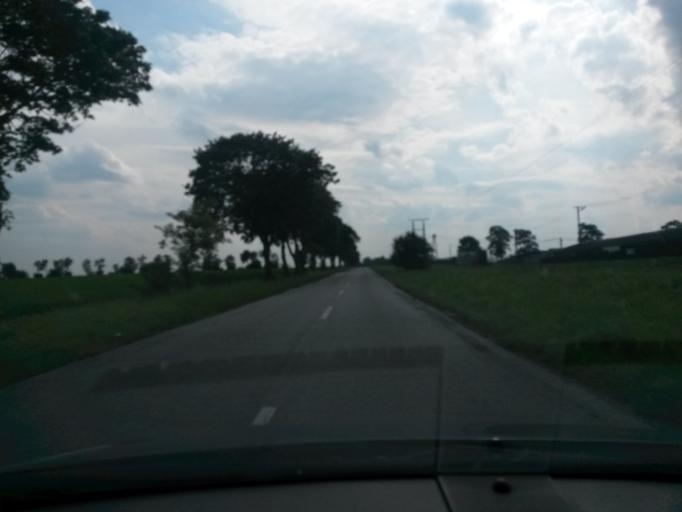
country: PL
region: Greater Poland Voivodeship
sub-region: Powiat poznanski
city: Kornik
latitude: 52.2906
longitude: 17.1168
